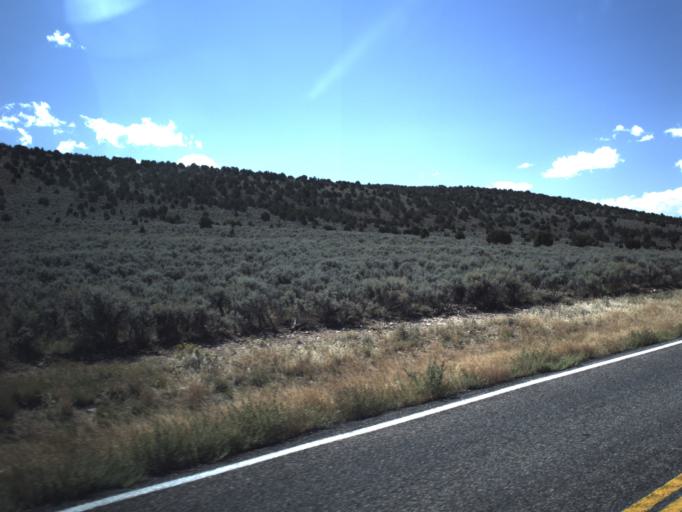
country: US
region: Utah
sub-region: Iron County
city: Parowan
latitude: 38.0540
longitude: -112.9729
